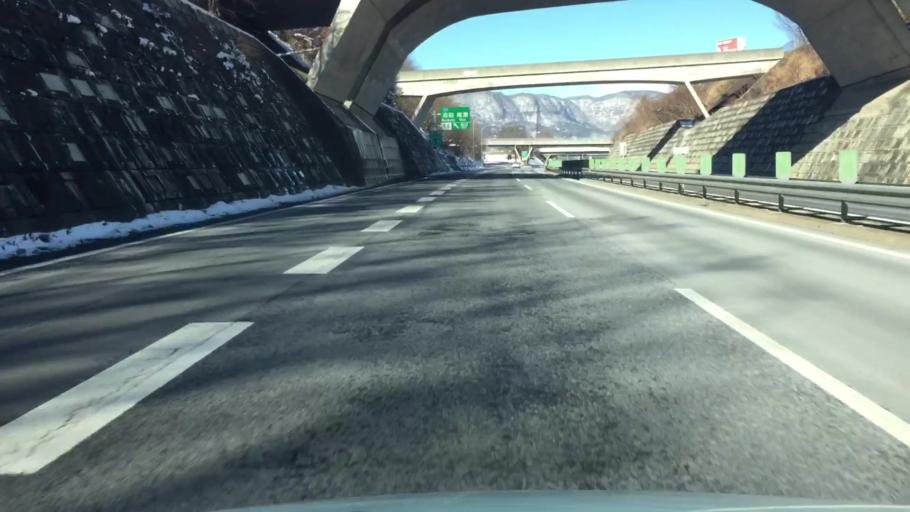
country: JP
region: Gunma
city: Numata
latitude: 36.6542
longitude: 139.0725
